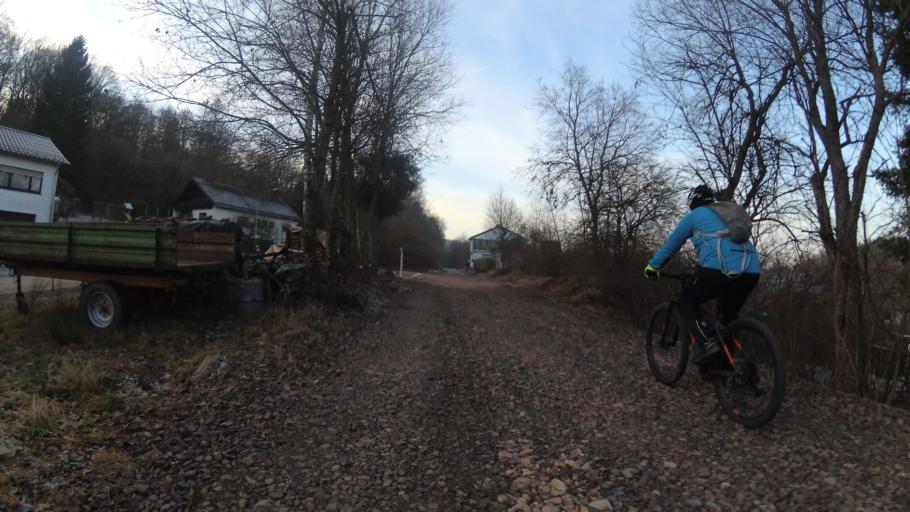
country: DE
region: Saarland
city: Nohfelden
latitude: 49.5807
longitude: 7.1439
